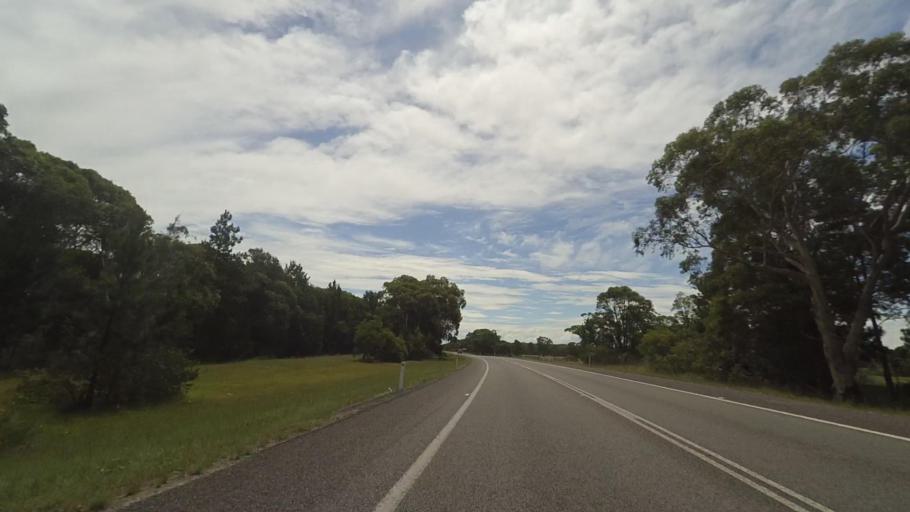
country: AU
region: New South Wales
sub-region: Port Stephens Shire
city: Medowie
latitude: -32.7865
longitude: 151.8986
